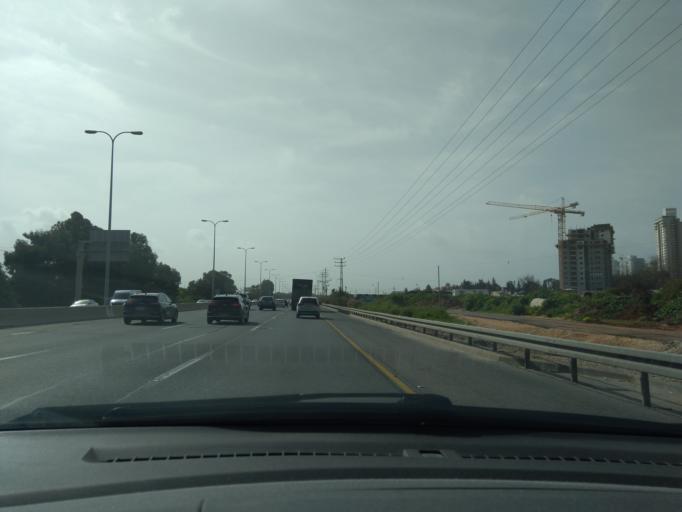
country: IL
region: Central District
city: Netanya
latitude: 32.3175
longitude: 34.8660
